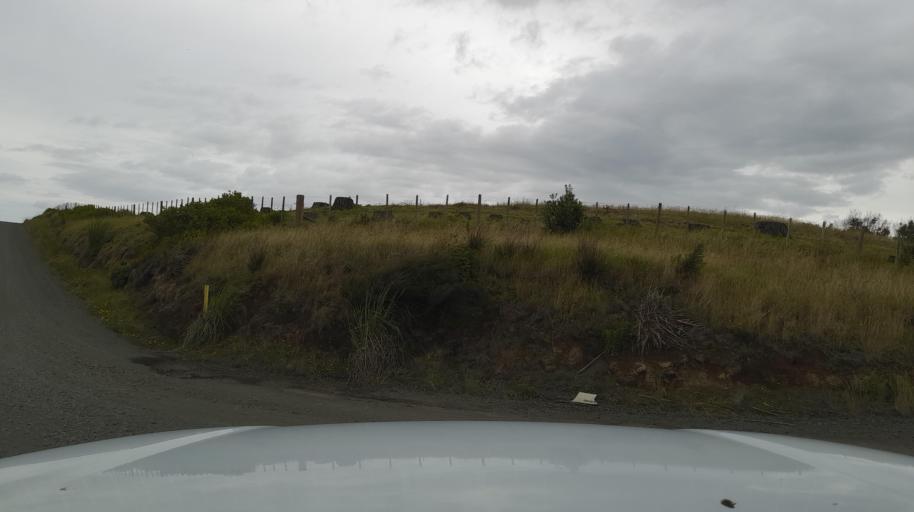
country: NZ
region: Northland
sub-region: Far North District
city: Ahipara
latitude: -35.1314
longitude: 173.1838
